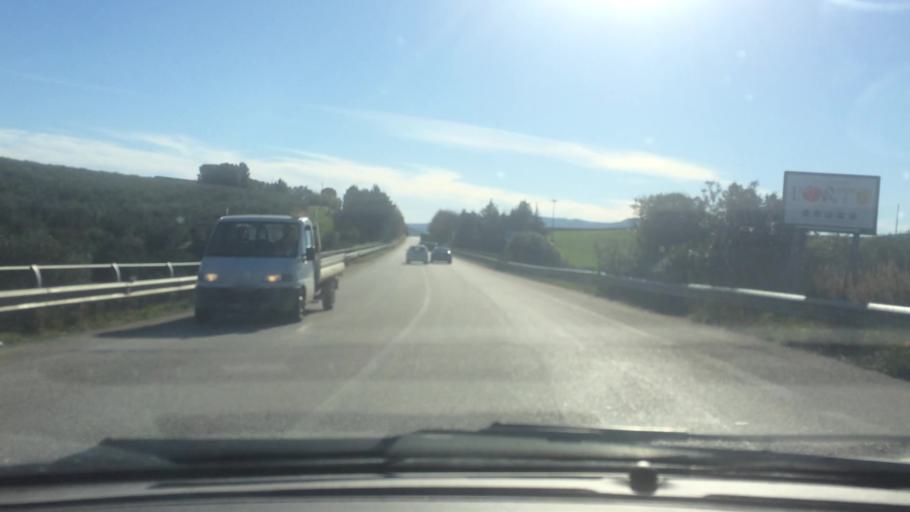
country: IT
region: Basilicate
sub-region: Provincia di Matera
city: Miglionico
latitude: 40.5919
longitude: 16.5735
